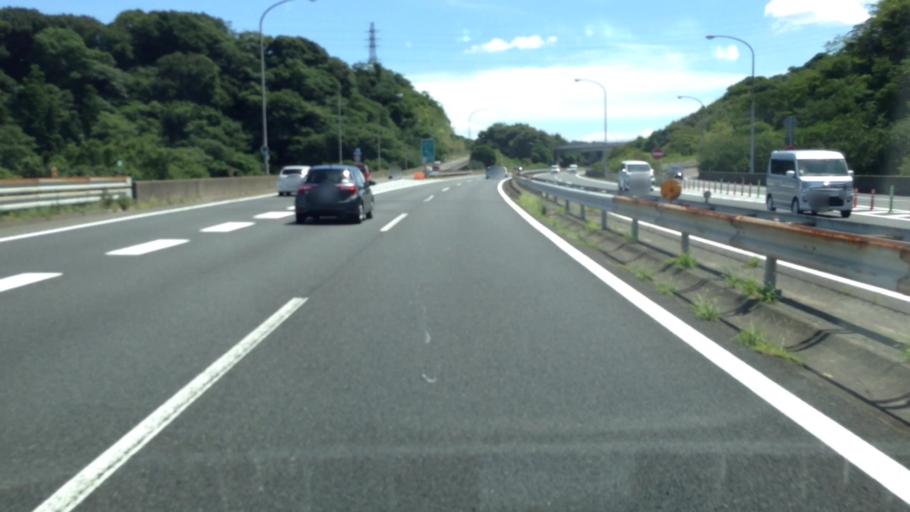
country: JP
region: Kanagawa
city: Yokosuka
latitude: 35.2797
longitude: 139.6317
